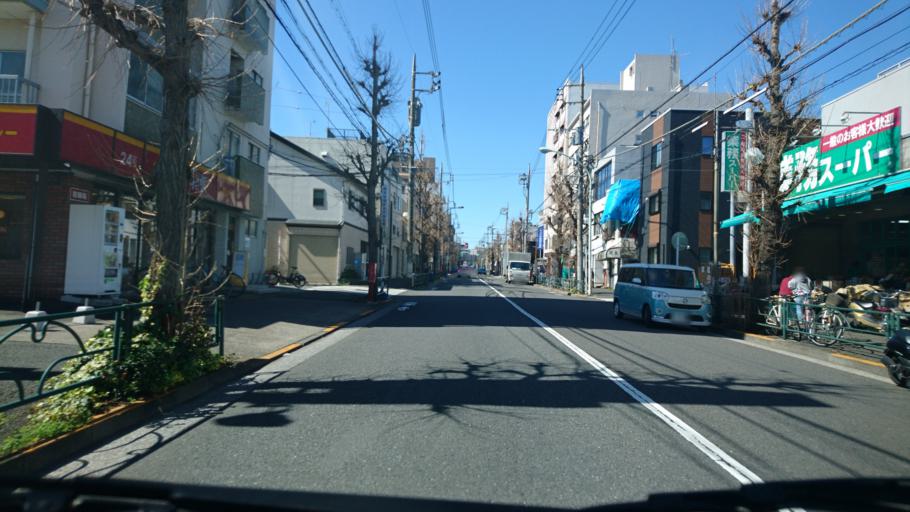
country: JP
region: Kanagawa
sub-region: Kawasaki-shi
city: Kawasaki
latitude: 35.5764
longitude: 139.7138
